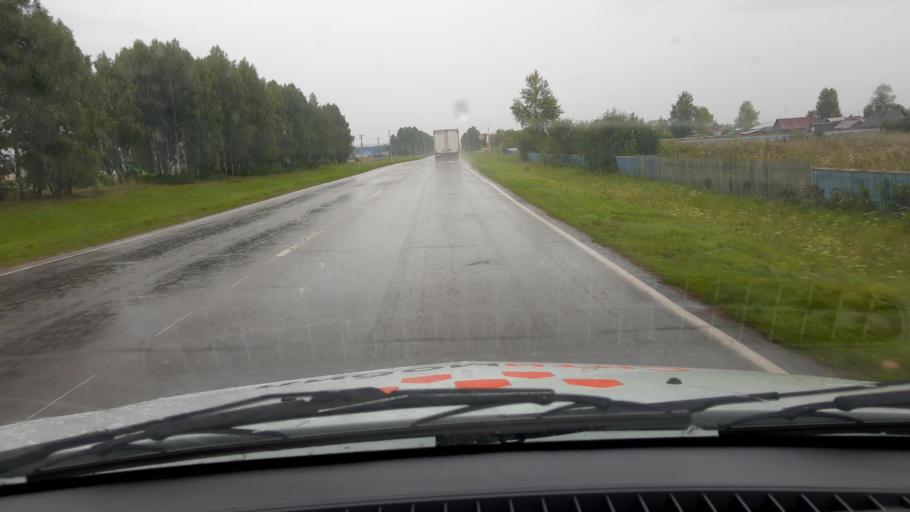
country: RU
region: Bashkortostan
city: Krasnaya Gorka
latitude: 55.0970
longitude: 56.6226
